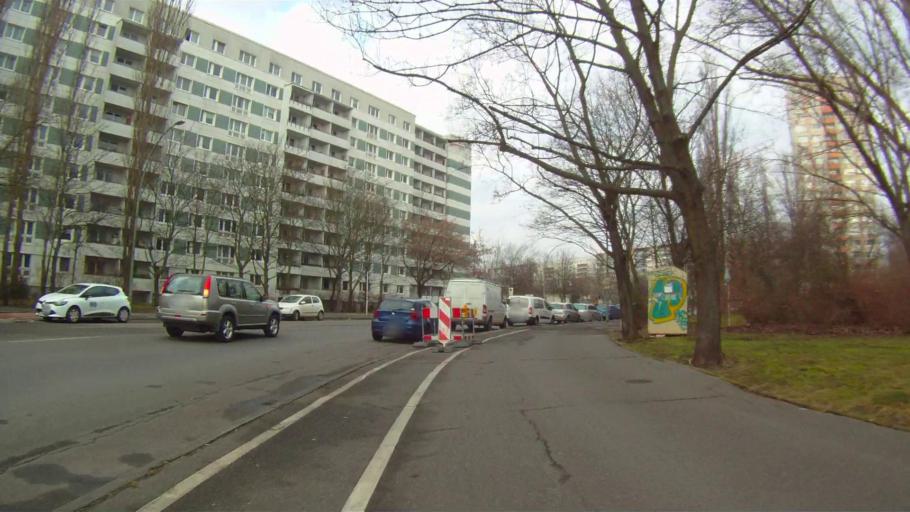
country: DE
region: Berlin
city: Friedrichsfelde
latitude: 52.4942
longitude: 13.5159
